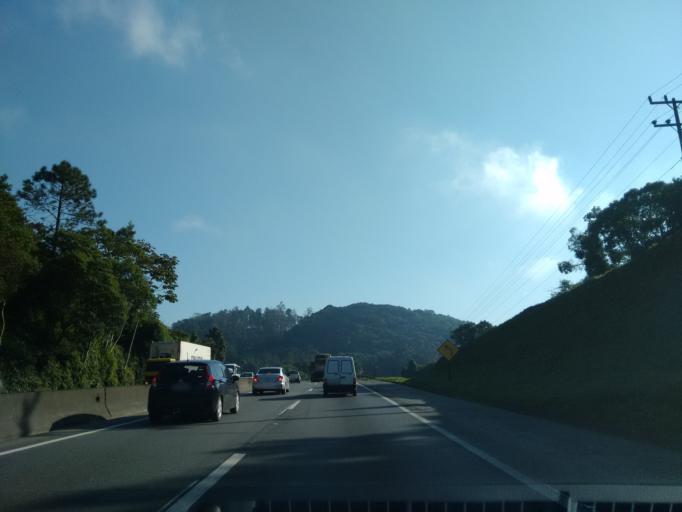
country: BR
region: Santa Catarina
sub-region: Joinville
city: Joinville
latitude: -26.2697
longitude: -48.8951
